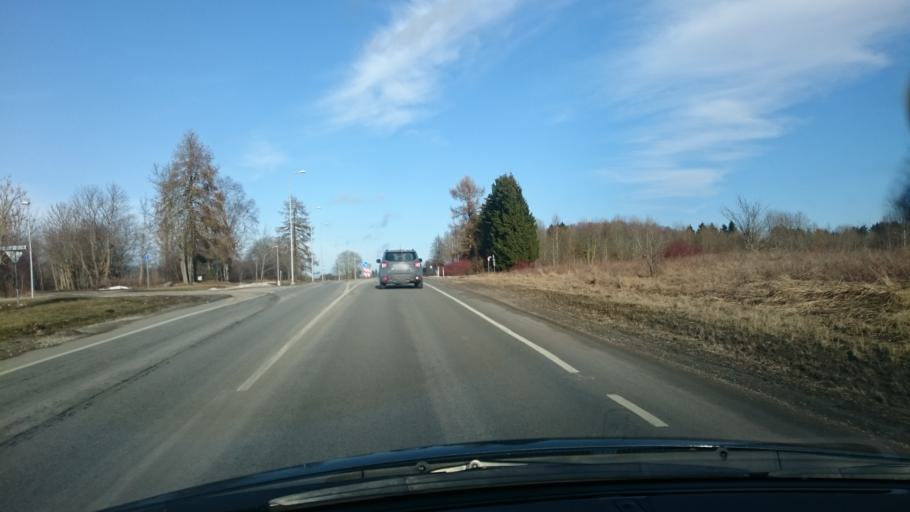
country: EE
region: Harju
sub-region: Keila linn
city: Keila
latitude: 59.4441
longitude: 24.3765
